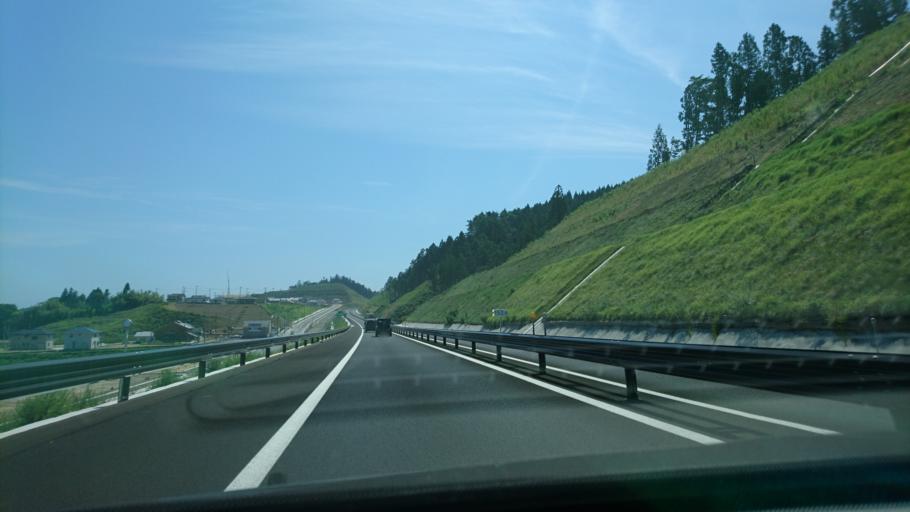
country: JP
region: Iwate
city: Ofunato
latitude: 39.0076
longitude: 141.6112
